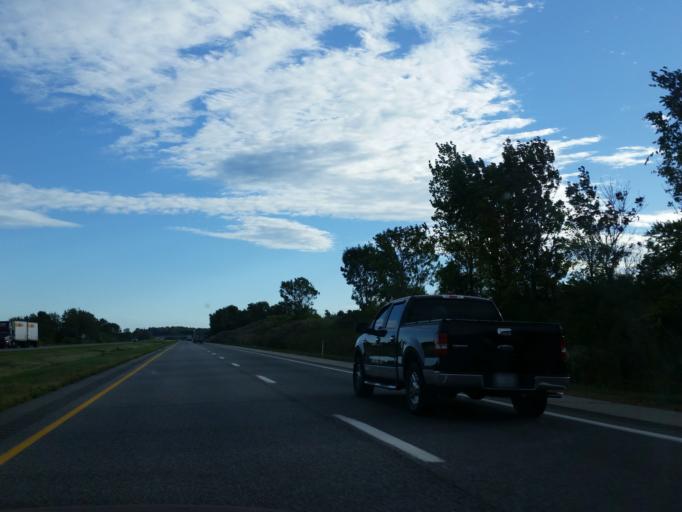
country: US
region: Pennsylvania
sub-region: Erie County
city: North East
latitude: 42.2164
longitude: -79.7947
